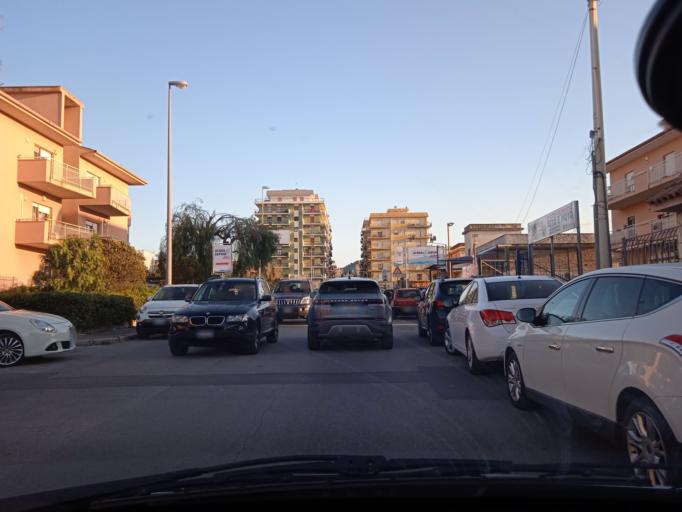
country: IT
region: Sicily
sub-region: Palermo
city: Bagheria
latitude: 38.0812
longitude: 13.5018
